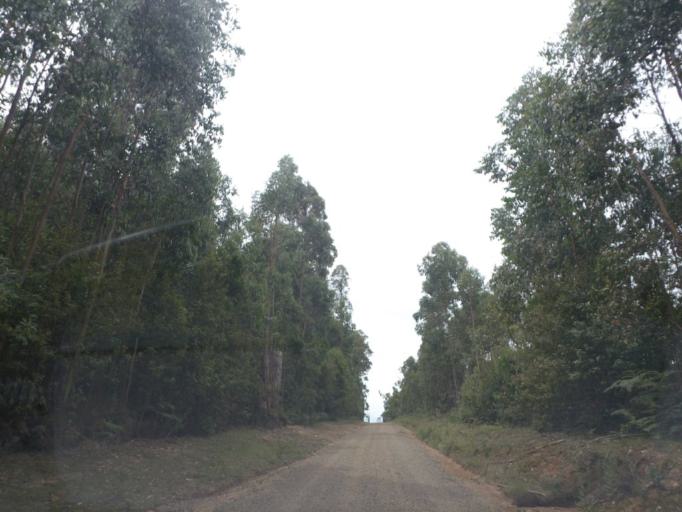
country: AU
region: Victoria
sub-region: Murrindindi
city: Alexandra
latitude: -37.4068
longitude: 145.5903
